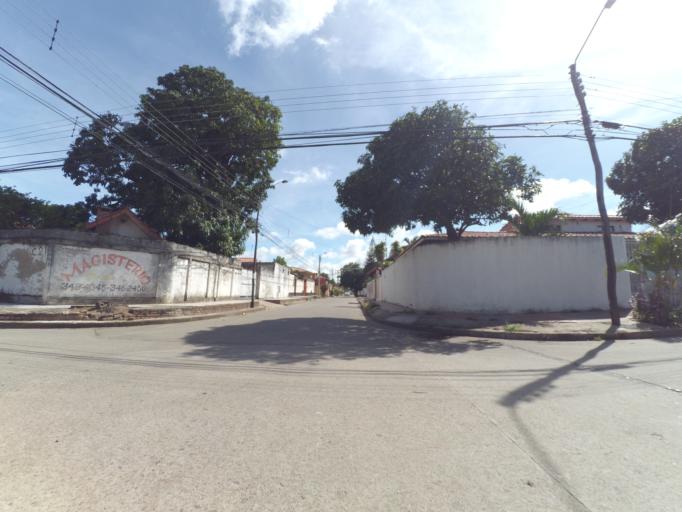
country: BO
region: Santa Cruz
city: Santa Cruz de la Sierra
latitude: -17.7598
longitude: -63.1561
